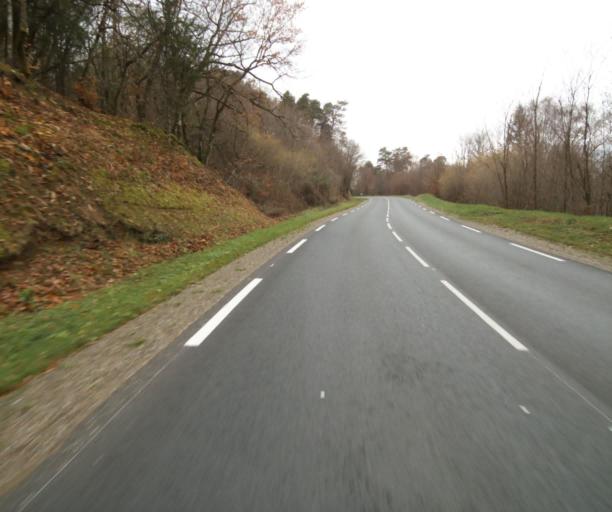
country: FR
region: Limousin
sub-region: Departement de la Correze
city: Tulle
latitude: 45.2661
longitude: 1.7342
